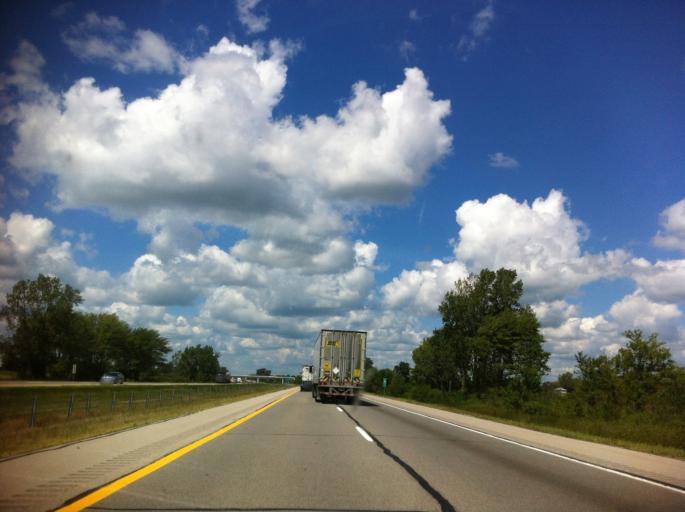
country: US
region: Michigan
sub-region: Monroe County
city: Dundee
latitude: 42.0062
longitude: -83.6784
